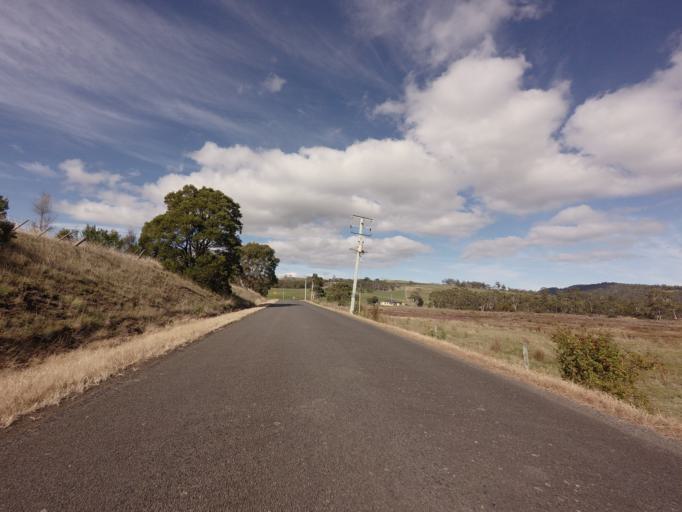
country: AU
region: Tasmania
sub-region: Clarence
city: Sandford
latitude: -43.0257
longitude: 147.7220
